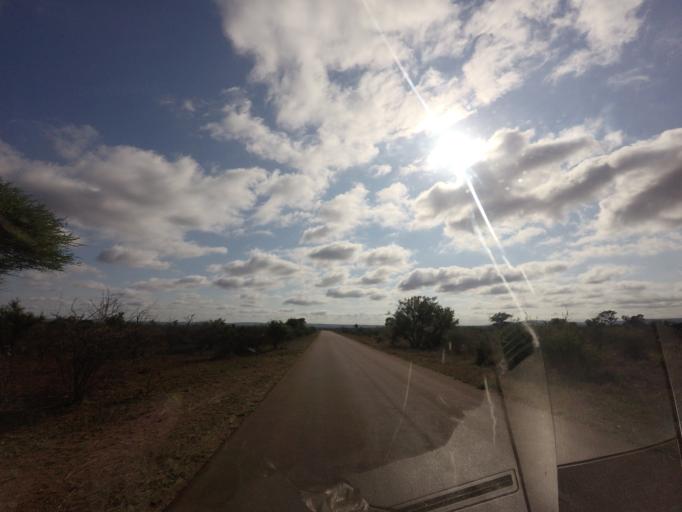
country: ZA
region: Mpumalanga
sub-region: Ehlanzeni District
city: Komatipoort
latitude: -25.1772
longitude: 31.9106
